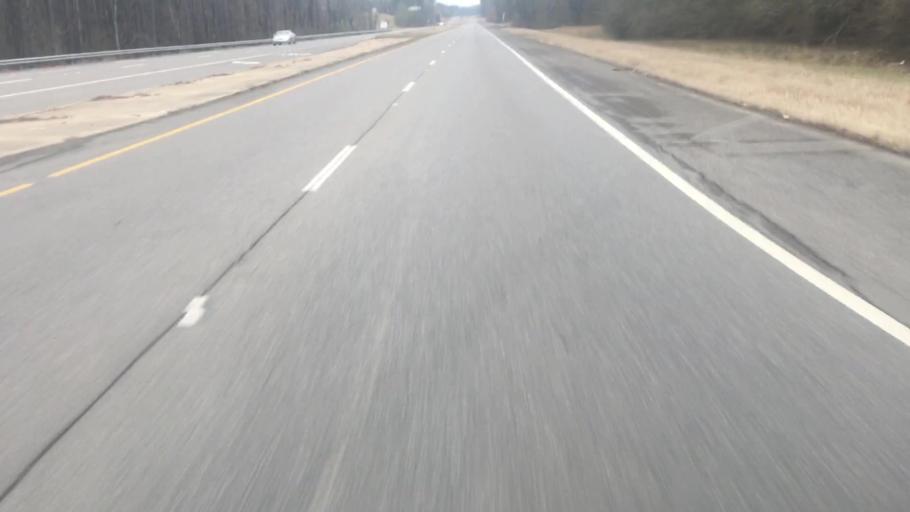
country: US
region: Alabama
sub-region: Walker County
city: Cordova
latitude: 33.8212
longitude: -87.1808
